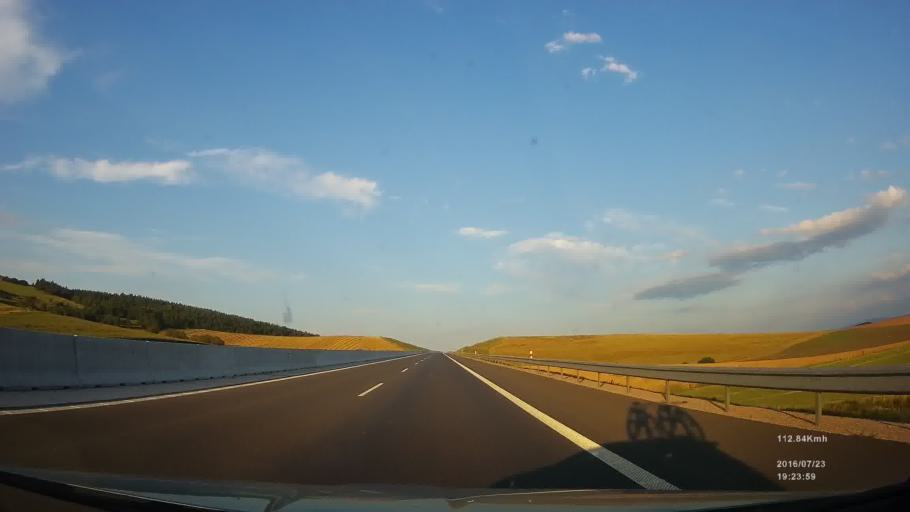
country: SK
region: Kosicky
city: Spisska Nova Ves
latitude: 49.0022
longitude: 20.4953
